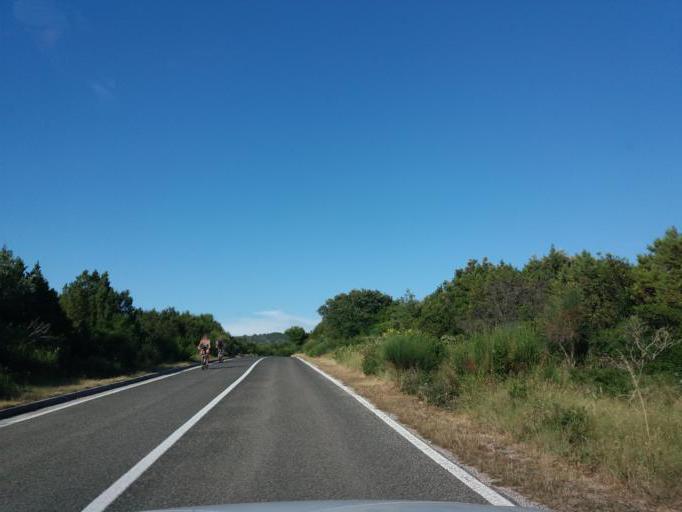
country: HR
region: Zadarska
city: Ugljan
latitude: 44.1343
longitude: 14.8638
